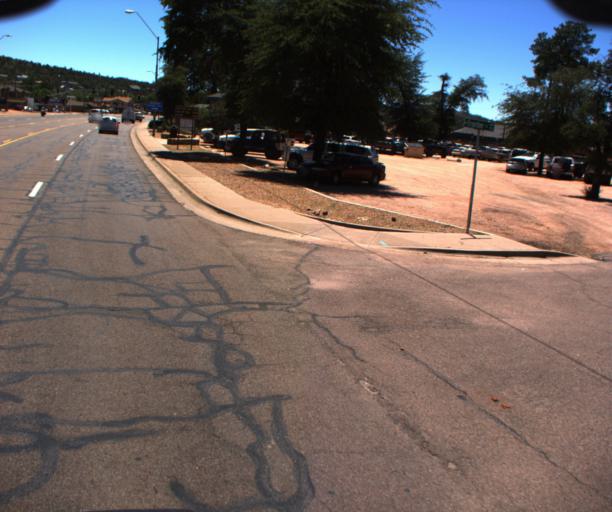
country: US
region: Arizona
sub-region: Gila County
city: Payson
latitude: 34.2320
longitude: -111.3243
